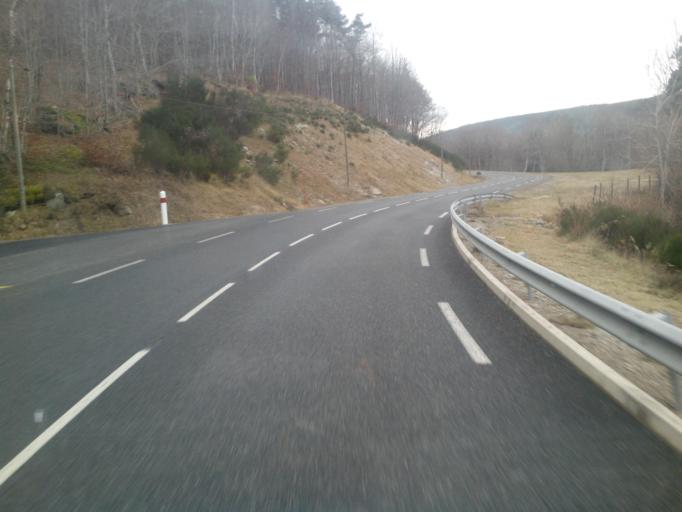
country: FR
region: Languedoc-Roussillon
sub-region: Departement de la Lozere
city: Mende
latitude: 44.5791
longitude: 3.4962
